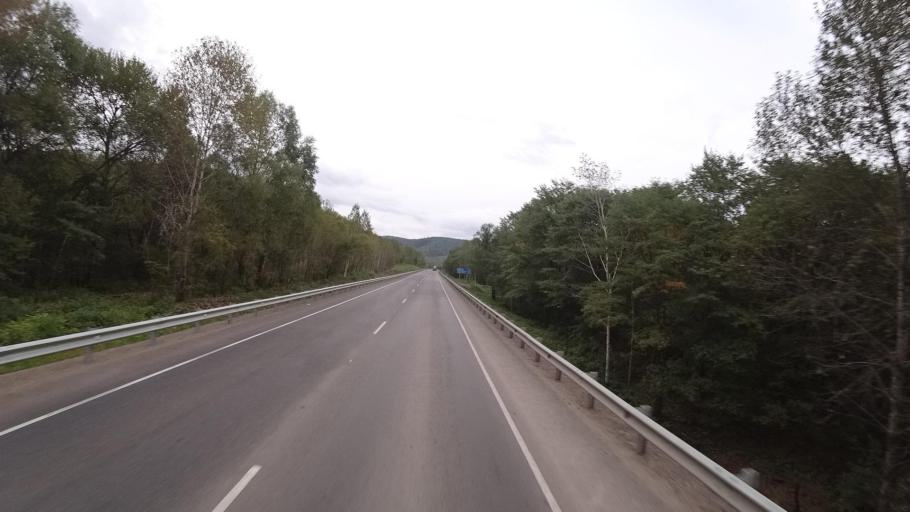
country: RU
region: Jewish Autonomous Oblast
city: Khingansk
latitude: 48.9858
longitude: 131.1389
